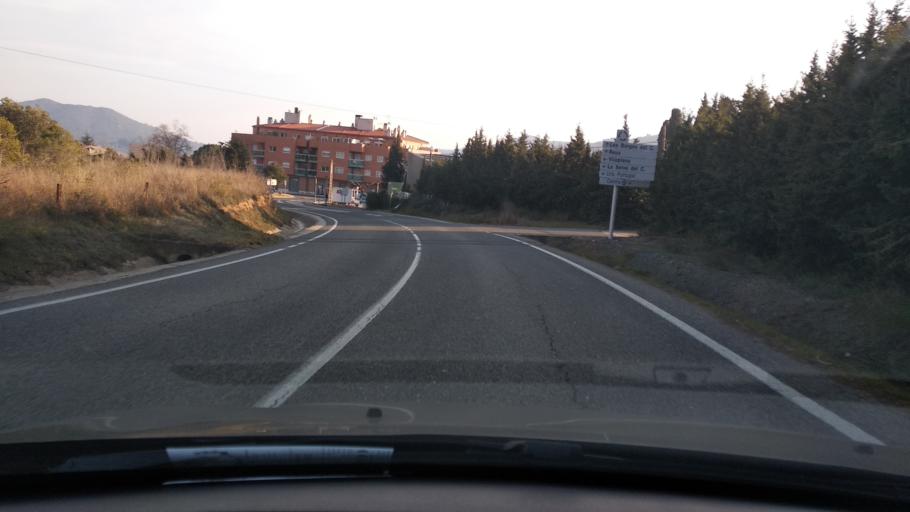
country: ES
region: Catalonia
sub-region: Provincia de Tarragona
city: Alforja
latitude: 41.2134
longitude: 0.9765
